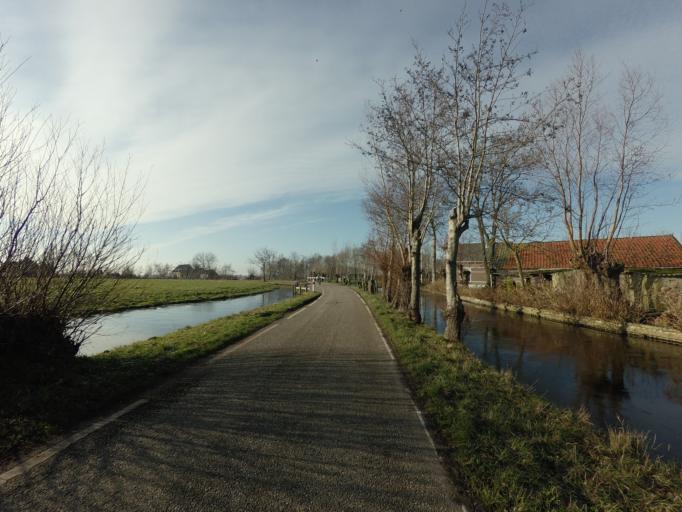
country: NL
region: South Holland
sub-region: Gemeente Vlist
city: Haastrecht
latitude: 52.0317
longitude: 4.7776
